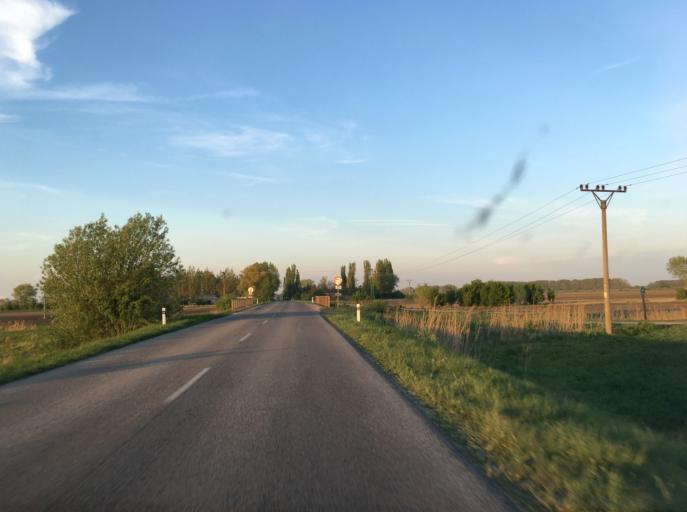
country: SK
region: Trnavsky
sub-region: Okres Dunajska Streda
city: Velky Meder
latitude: 47.8966
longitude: 17.8438
